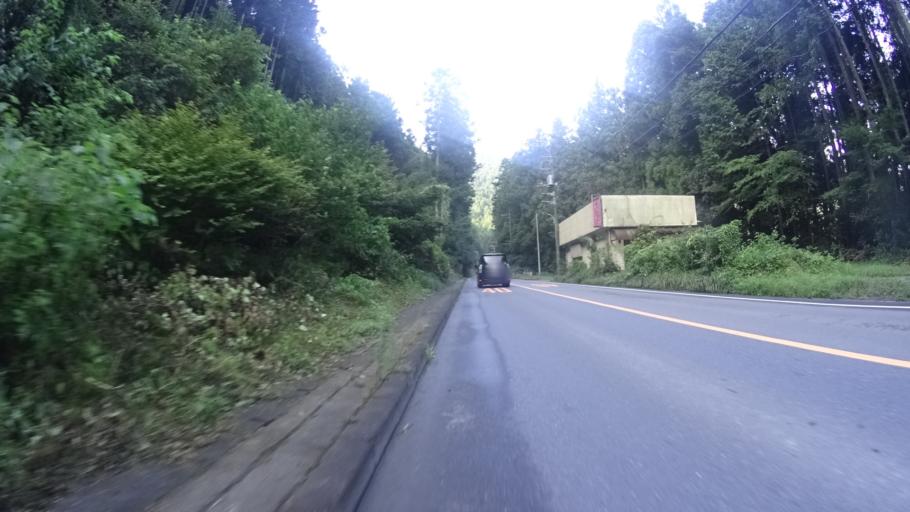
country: JP
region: Tokyo
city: Ome
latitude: 35.8099
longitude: 139.1641
